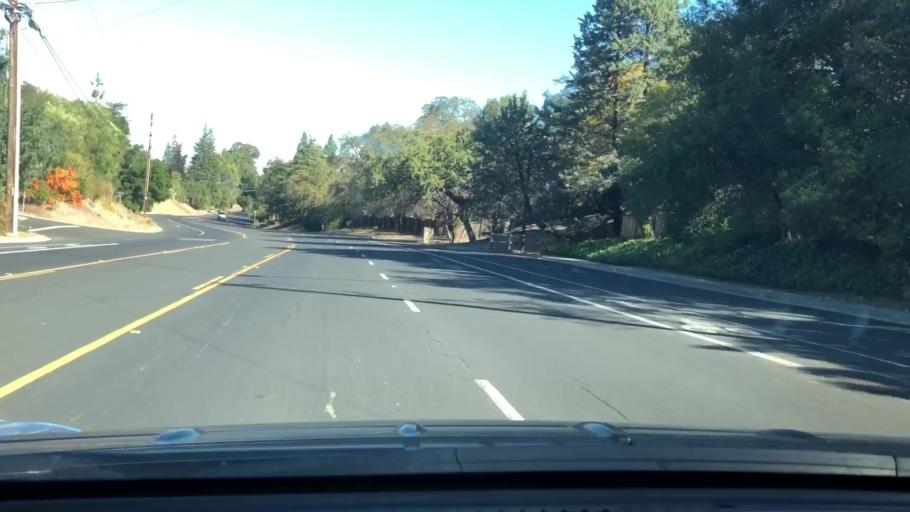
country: US
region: California
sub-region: Santa Clara County
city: Los Gatos
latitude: 37.2479
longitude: -121.9715
